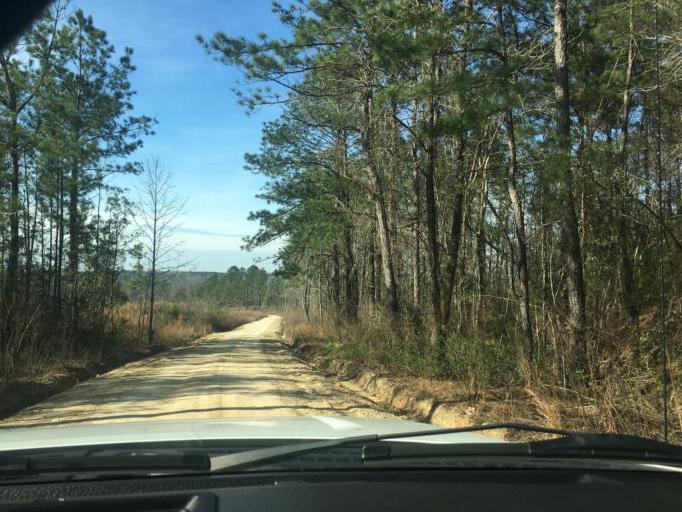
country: US
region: Alabama
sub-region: Lee County
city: Auburn
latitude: 32.4313
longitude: -85.4612
